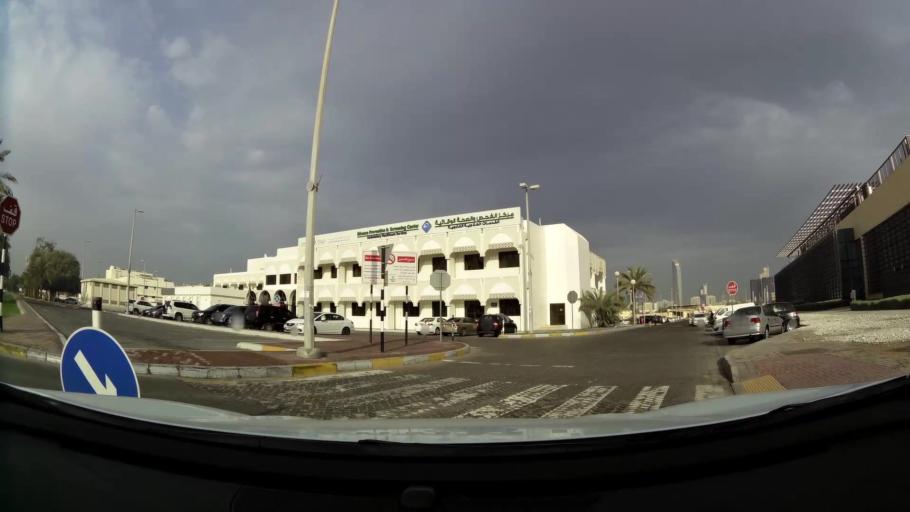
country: AE
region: Abu Dhabi
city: Abu Dhabi
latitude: 24.4690
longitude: 54.3688
